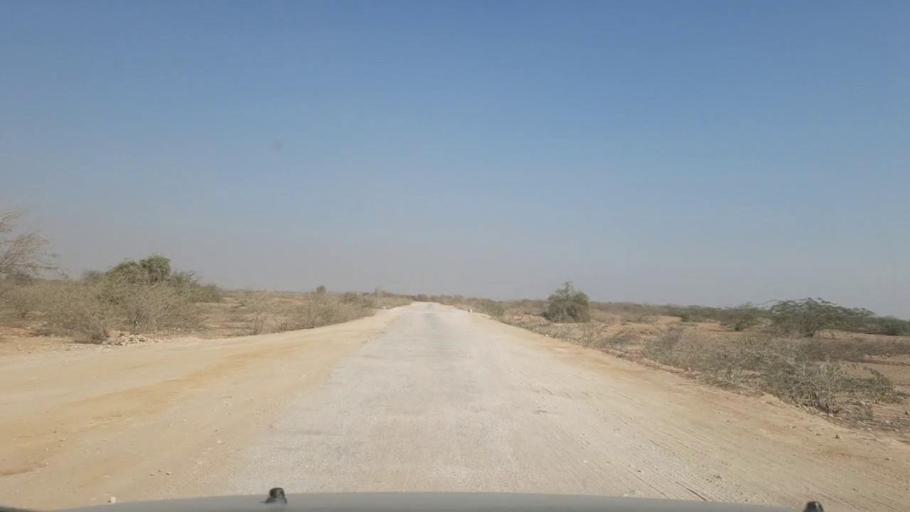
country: PK
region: Sindh
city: Thatta
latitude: 24.9130
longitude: 67.9333
